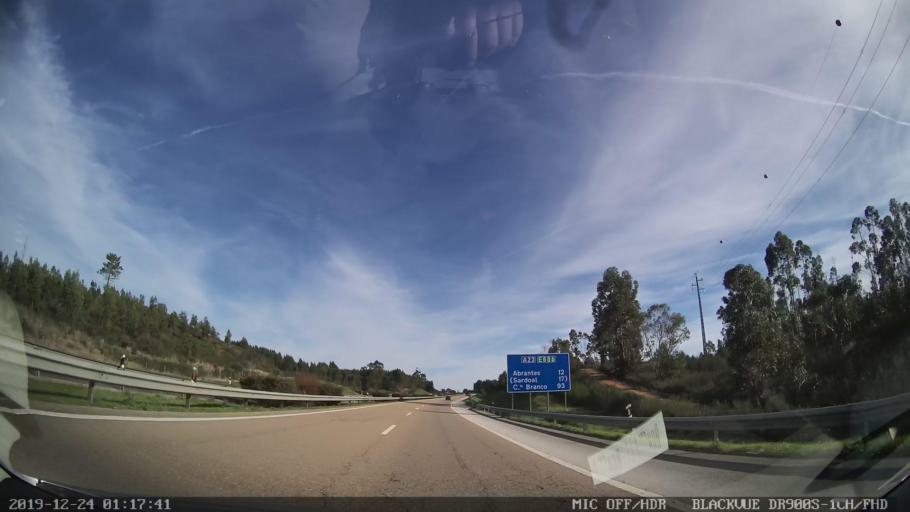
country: PT
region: Santarem
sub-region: Constancia
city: Constancia
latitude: 39.4873
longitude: -8.3194
